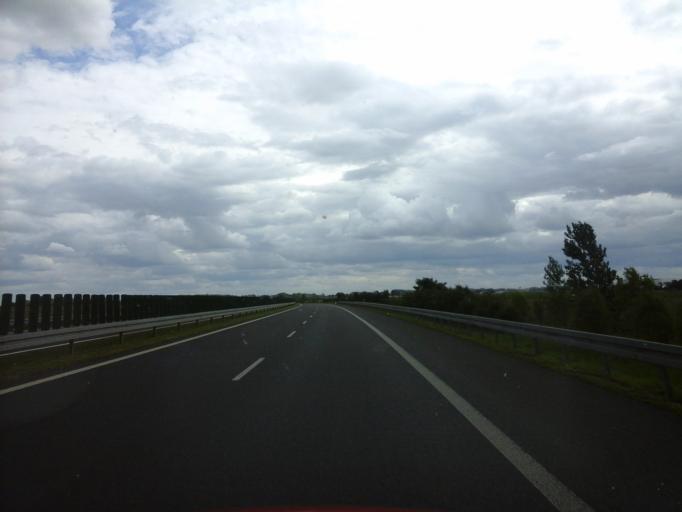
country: PL
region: West Pomeranian Voivodeship
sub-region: Powiat pyrzycki
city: Warnice
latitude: 53.3196
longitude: 14.9709
